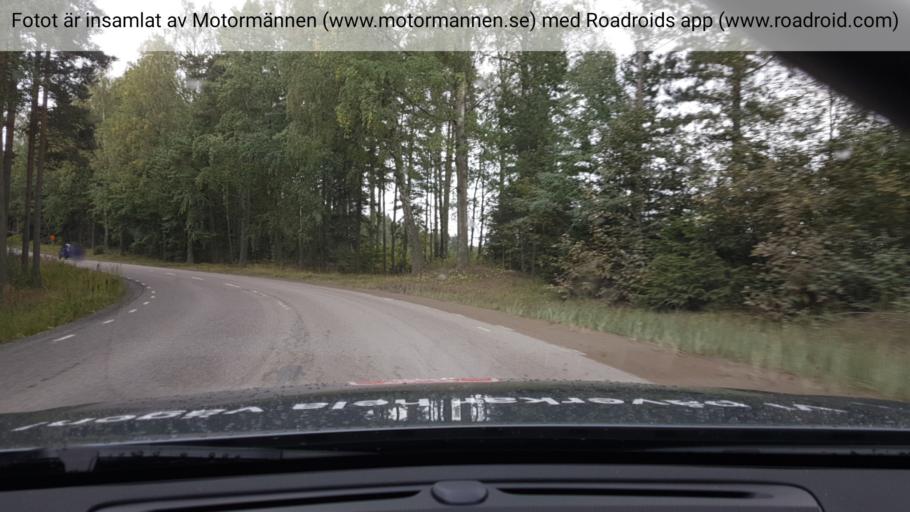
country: SE
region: Stockholm
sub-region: Botkyrka Kommun
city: Tullinge
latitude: 59.1569
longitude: 17.9281
